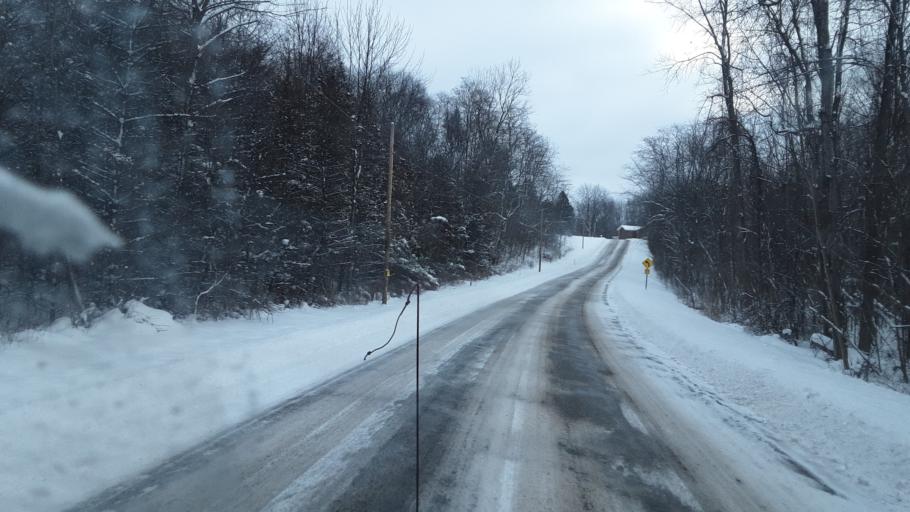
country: US
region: New York
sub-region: Wayne County
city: Lyons
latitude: 43.1392
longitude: -76.9970
